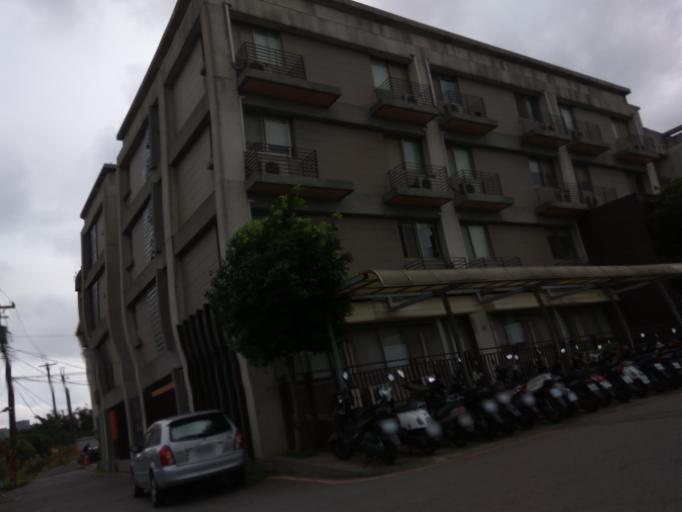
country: TW
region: Taiwan
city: Taoyuan City
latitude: 24.9913
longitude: 121.2304
